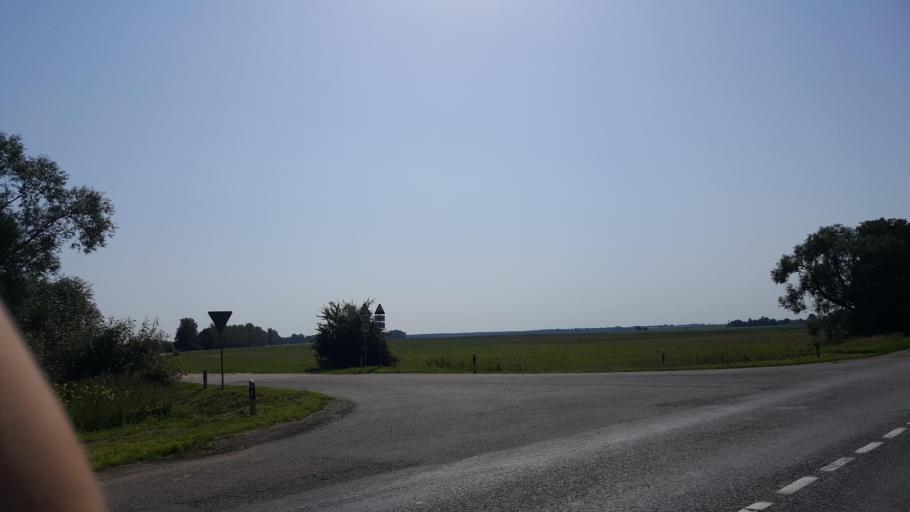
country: BY
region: Brest
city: Zhabinka
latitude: 52.2376
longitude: 23.9792
